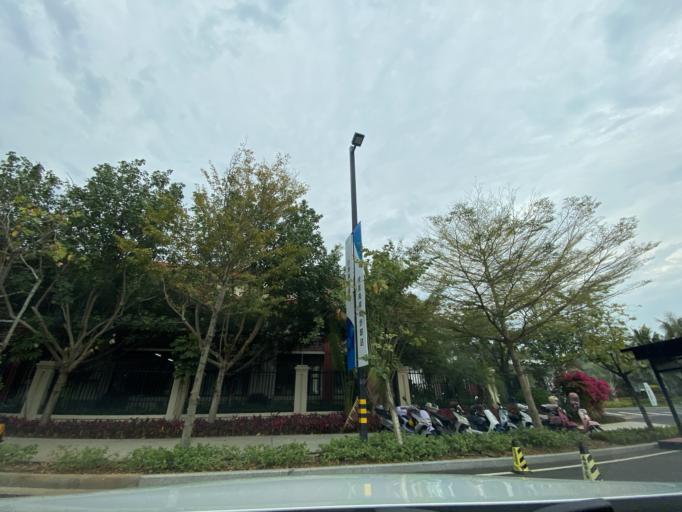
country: CN
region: Hainan
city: Yingzhou
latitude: 18.4036
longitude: 109.8573
